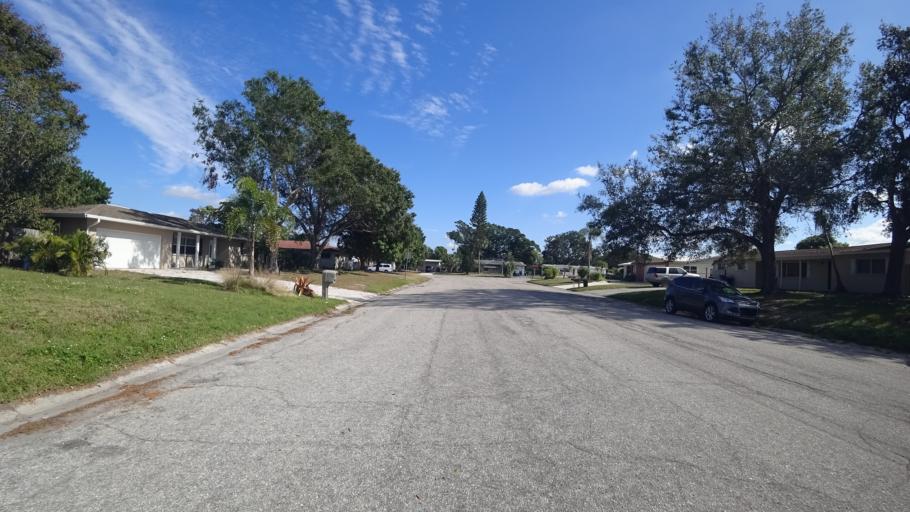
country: US
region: Florida
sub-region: Manatee County
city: West Bradenton
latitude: 27.4988
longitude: -82.6251
